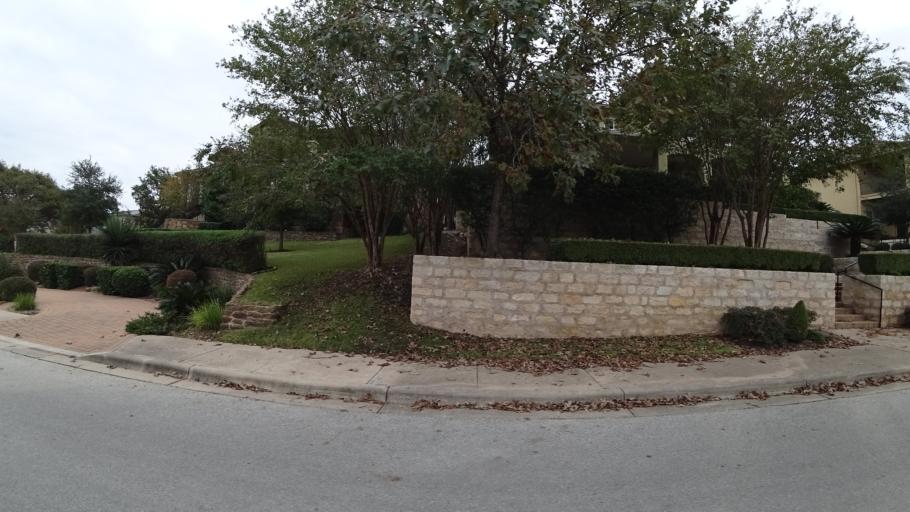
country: US
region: Texas
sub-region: Travis County
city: Bee Cave
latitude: 30.3209
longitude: -97.9182
